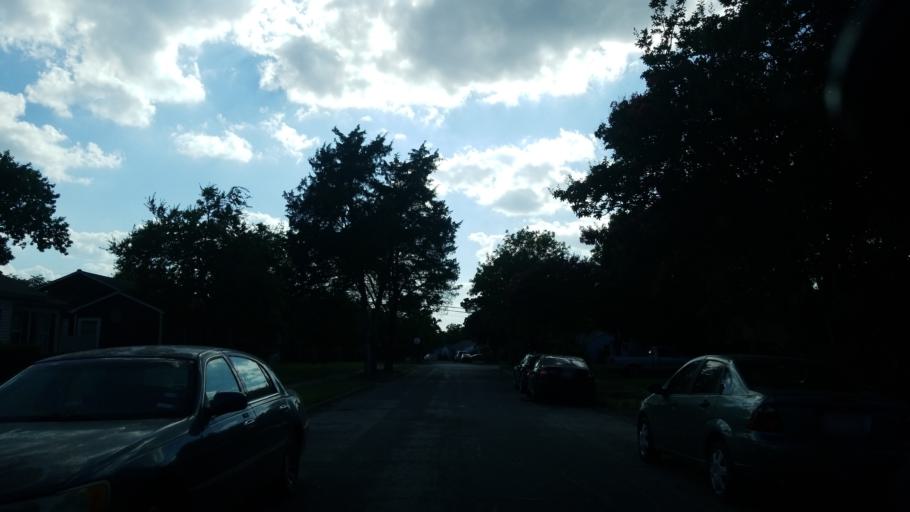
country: US
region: Texas
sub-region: Dallas County
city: Balch Springs
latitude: 32.7665
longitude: -96.7081
